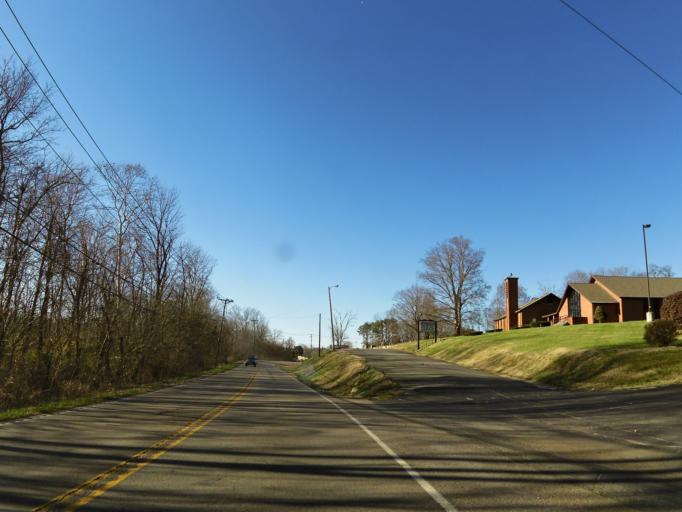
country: US
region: Tennessee
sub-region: Knox County
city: Knoxville
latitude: 36.0365
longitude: -83.9999
